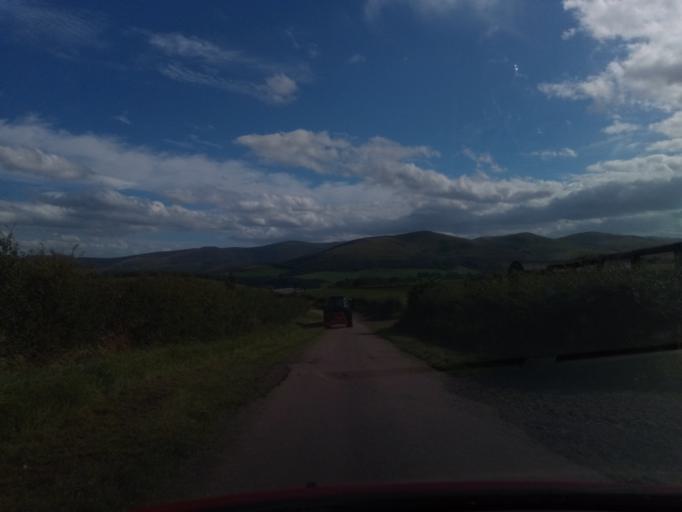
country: GB
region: England
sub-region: Northumberland
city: Kirknewton
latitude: 55.6011
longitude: -2.1871
